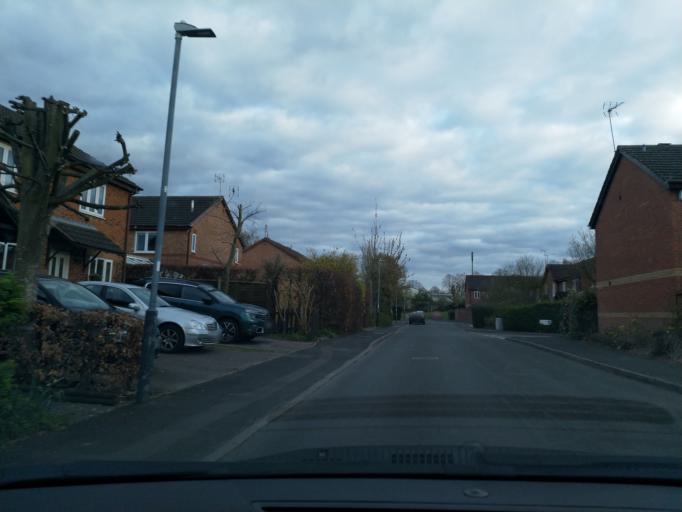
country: GB
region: England
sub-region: Warwickshire
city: Royal Leamington Spa
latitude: 52.2836
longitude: -1.5256
